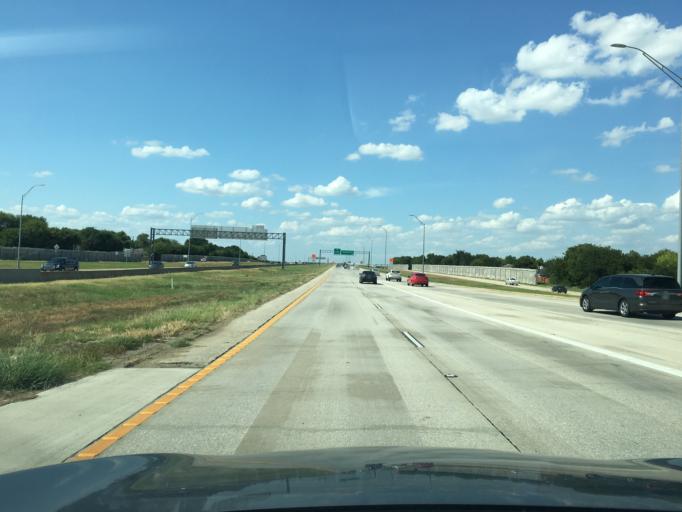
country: US
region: Texas
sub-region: Tarrant County
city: Arlington
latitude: 32.6525
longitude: -97.0616
